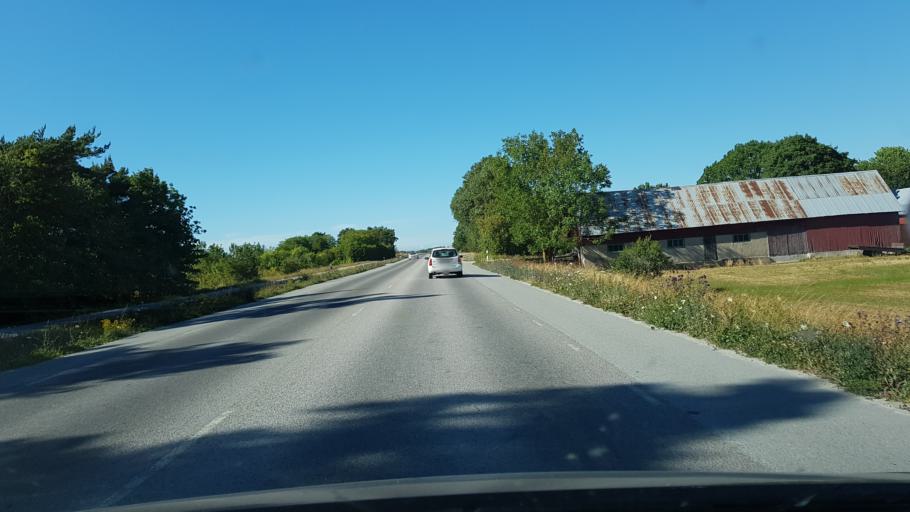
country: SE
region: Gotland
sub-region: Gotland
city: Vibble
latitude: 57.5700
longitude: 18.2082
